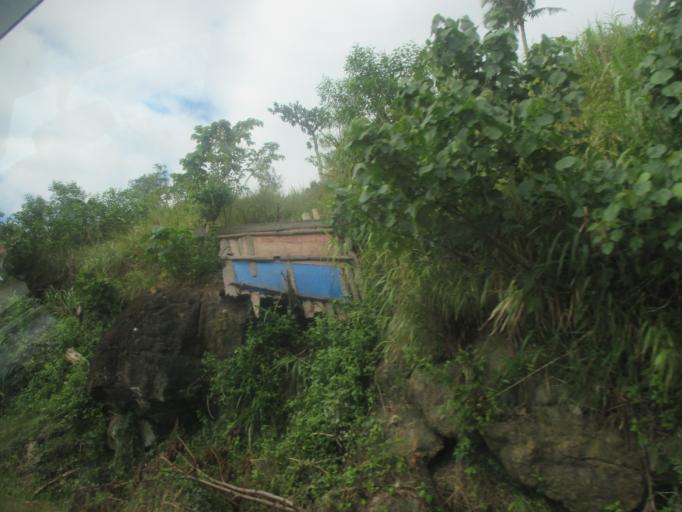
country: PH
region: Eastern Visayas
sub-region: Province of Eastern Samar
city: Lawa-an
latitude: 11.1210
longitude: 125.2451
